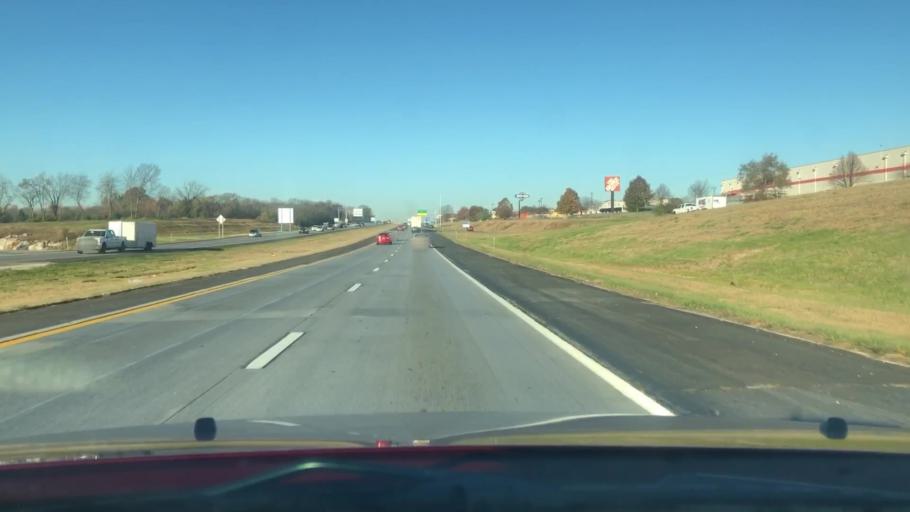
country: US
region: Missouri
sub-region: Greene County
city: Springfield
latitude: 37.1394
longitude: -93.2540
